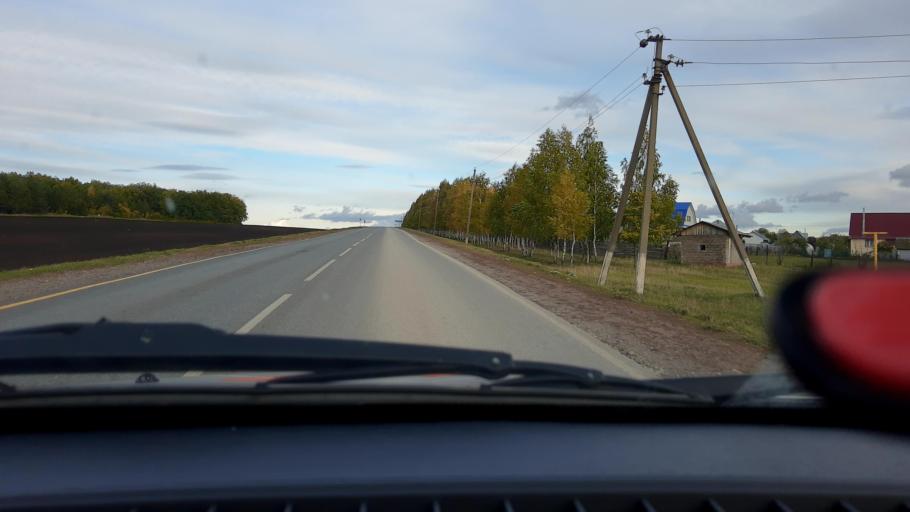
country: RU
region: Bashkortostan
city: Avdon
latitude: 54.5608
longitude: 55.6607
